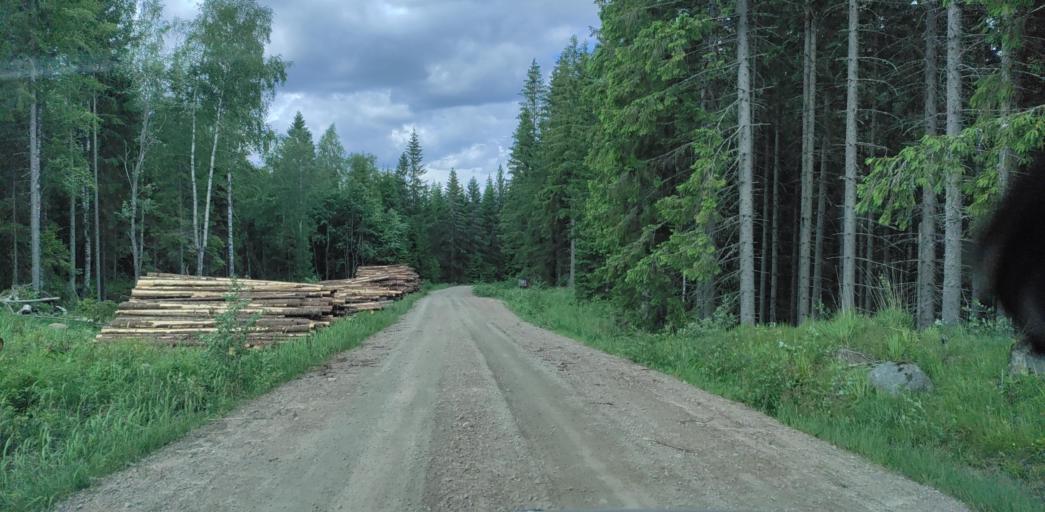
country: SE
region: Vaermland
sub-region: Munkfors Kommun
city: Munkfors
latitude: 59.9597
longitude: 13.4136
